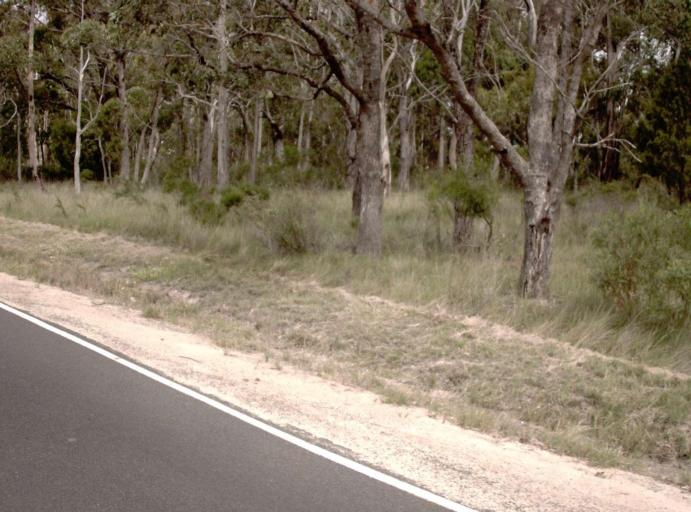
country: AU
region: Victoria
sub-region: Latrobe
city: Traralgon
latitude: -38.3816
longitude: 146.7660
